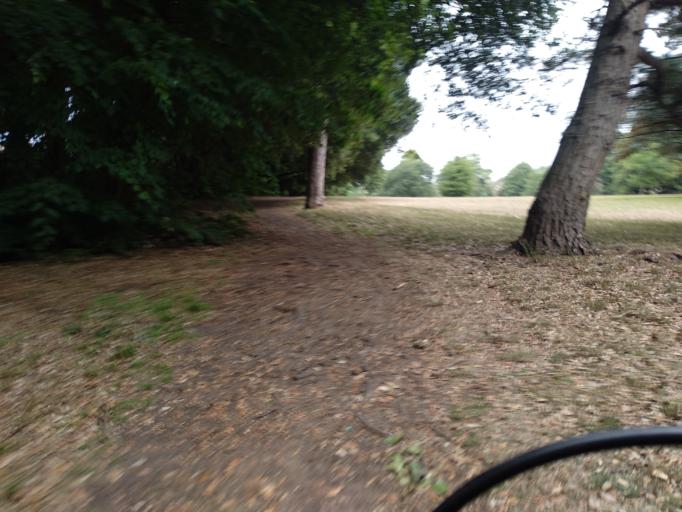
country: GB
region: England
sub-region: Isle of Wight
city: Sandown
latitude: 50.6539
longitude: -1.1649
